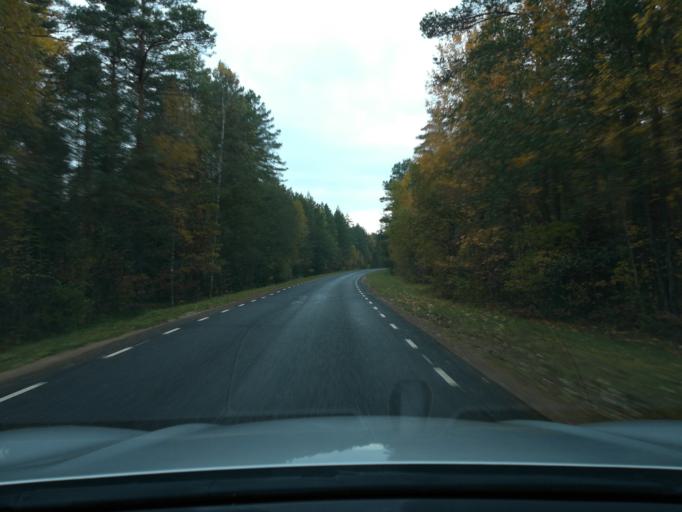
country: EE
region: Ida-Virumaa
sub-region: Johvi vald
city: Johvi
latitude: 59.0298
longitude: 27.3911
